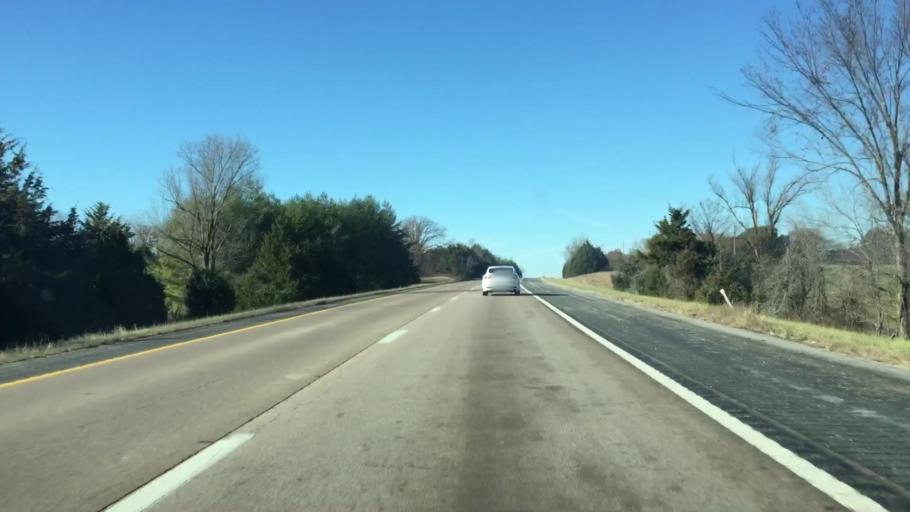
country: US
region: Missouri
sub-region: Miller County
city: Eldon
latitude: 38.3684
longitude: -92.4726
